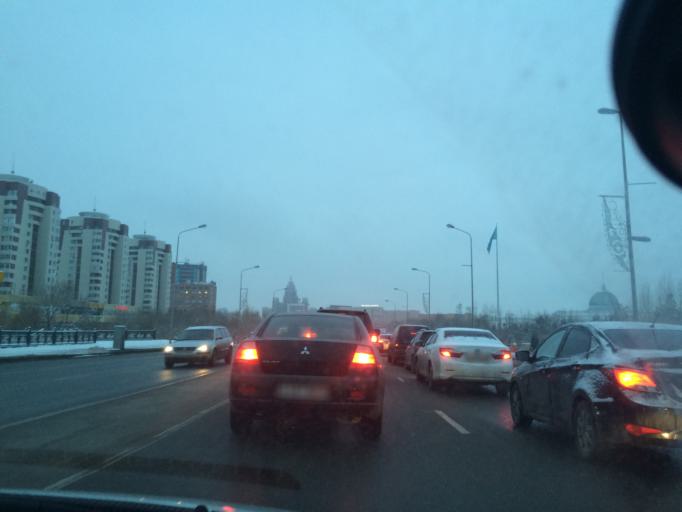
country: KZ
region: Astana Qalasy
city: Astana
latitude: 51.1514
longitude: 71.4275
